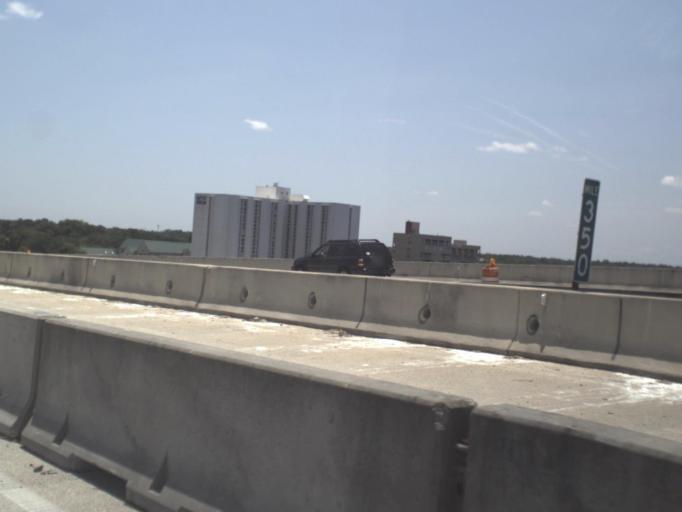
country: US
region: Florida
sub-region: Duval County
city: Jacksonville
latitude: 30.3140
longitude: -81.6665
